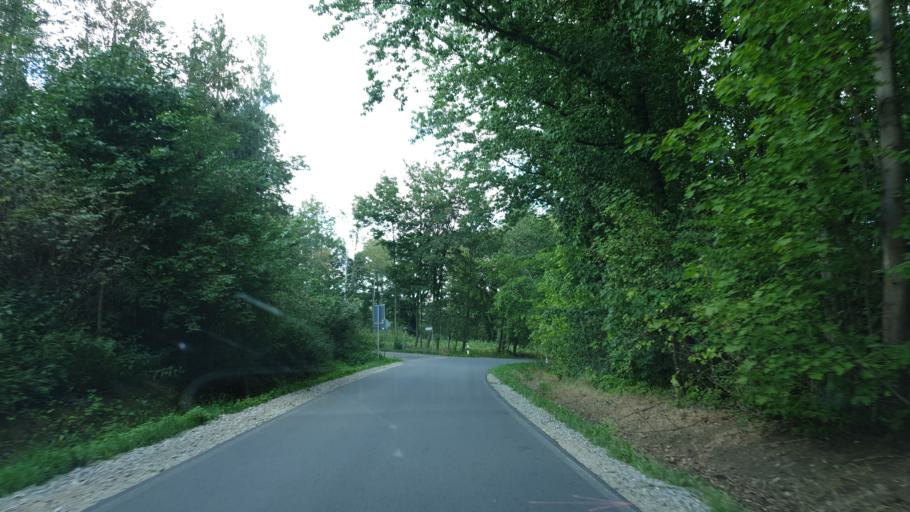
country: DE
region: Saxony
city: Lichtenstein
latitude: 50.7170
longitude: 12.6383
